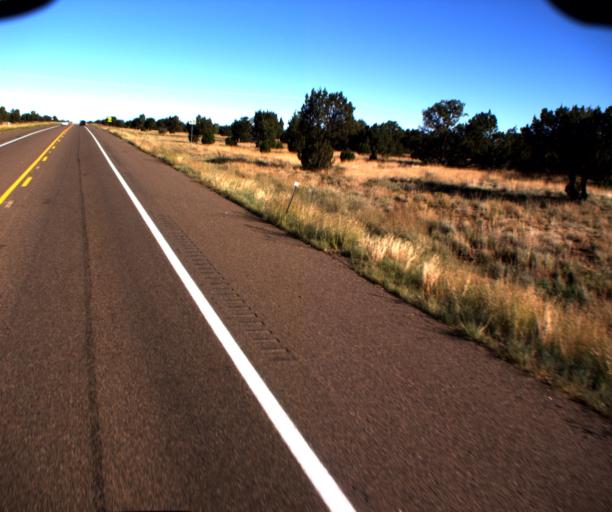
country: US
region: Arizona
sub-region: Navajo County
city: Show Low
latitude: 34.2731
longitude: -110.0242
